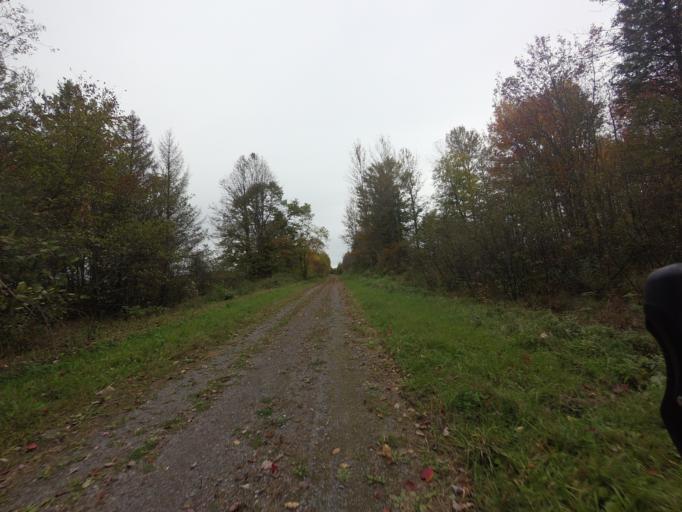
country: CA
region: Quebec
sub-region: Outaouais
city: Shawville
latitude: 45.6287
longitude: -76.5090
